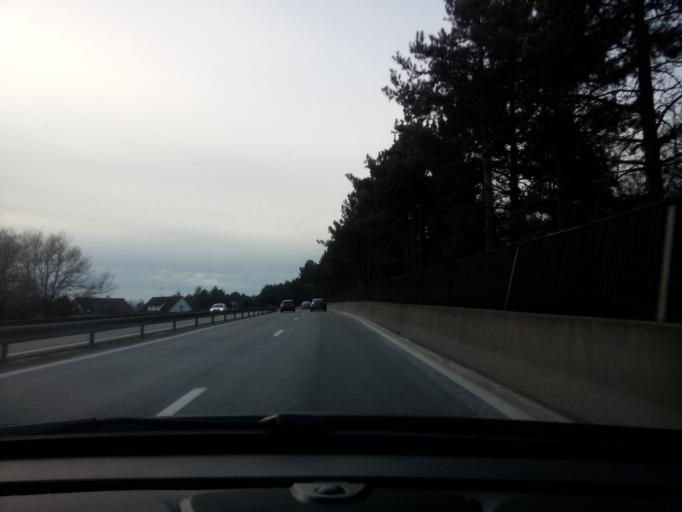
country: FR
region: Centre
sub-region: Departement du Loiret
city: Saran
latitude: 47.9465
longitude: 1.8751
